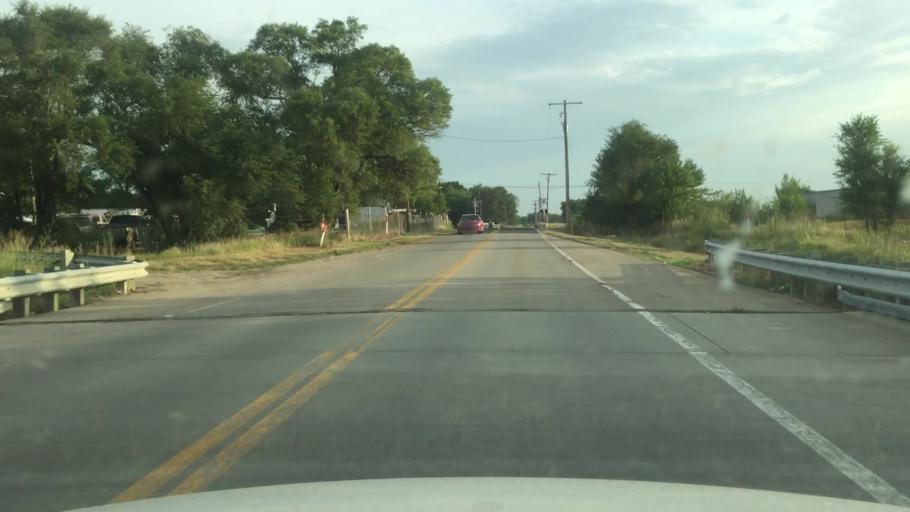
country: US
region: Kansas
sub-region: Shawnee County
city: Topeka
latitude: 39.0547
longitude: -95.6131
